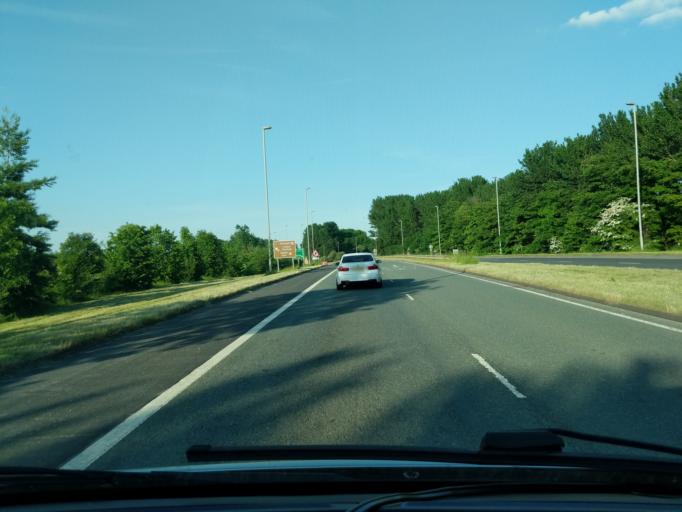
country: GB
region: England
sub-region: Borough of Halton
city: Runcorn
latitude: 53.3384
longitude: -2.7465
